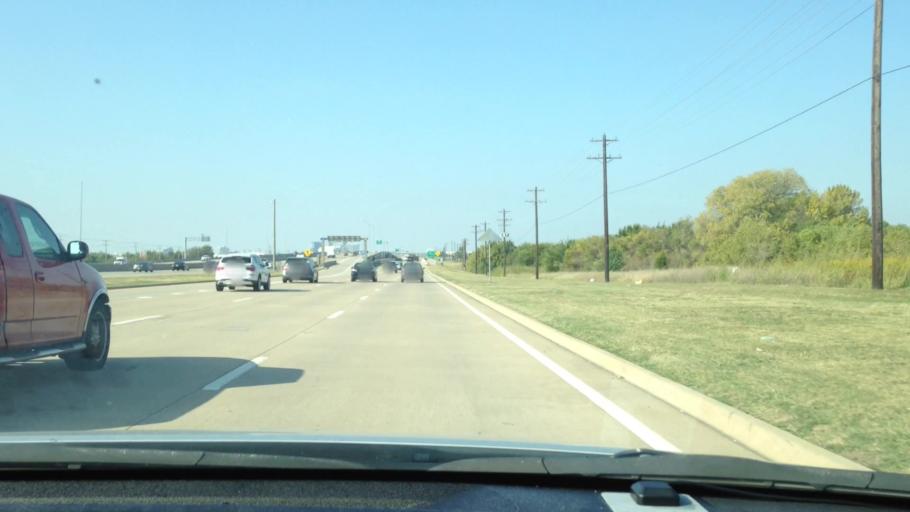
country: US
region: Texas
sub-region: Collin County
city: Frisco
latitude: 33.1079
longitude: -96.7801
